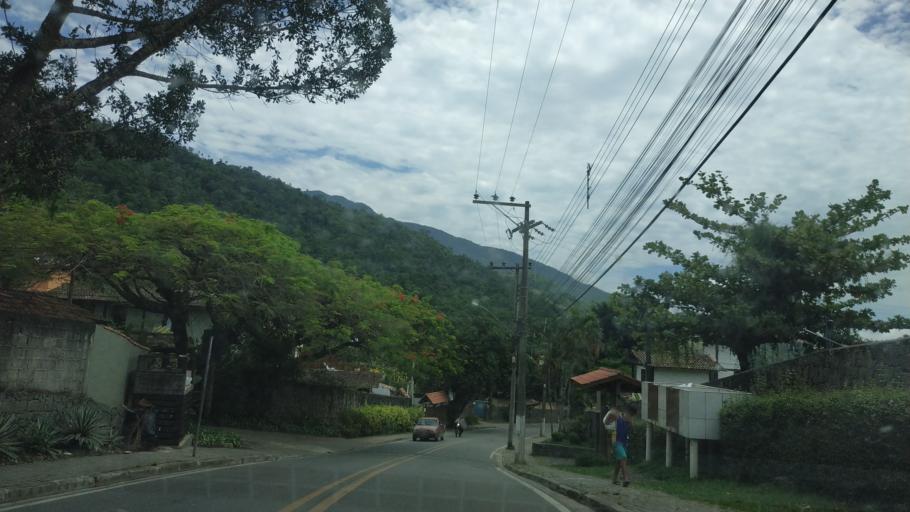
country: BR
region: Sao Paulo
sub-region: Ilhabela
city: Ilhabela
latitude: -23.8275
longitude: -45.3529
